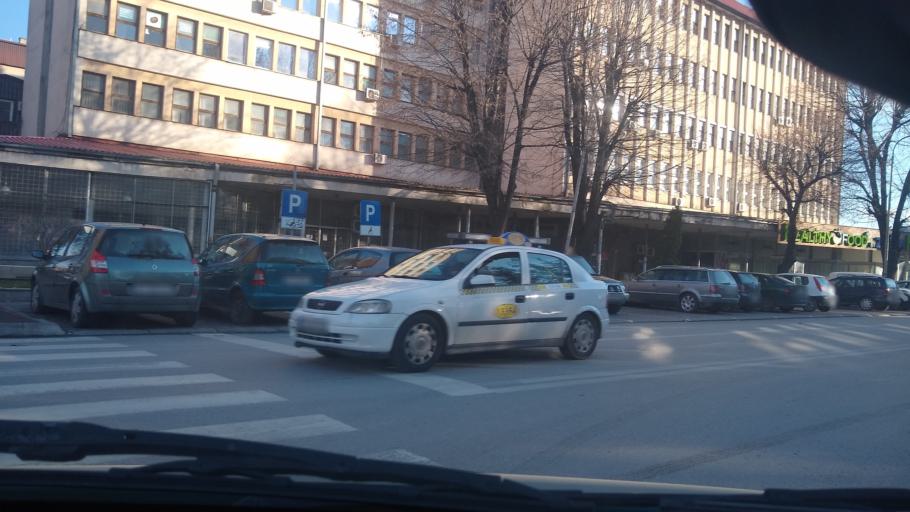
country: MK
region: Bitola
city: Bitola
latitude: 41.0313
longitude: 21.3354
